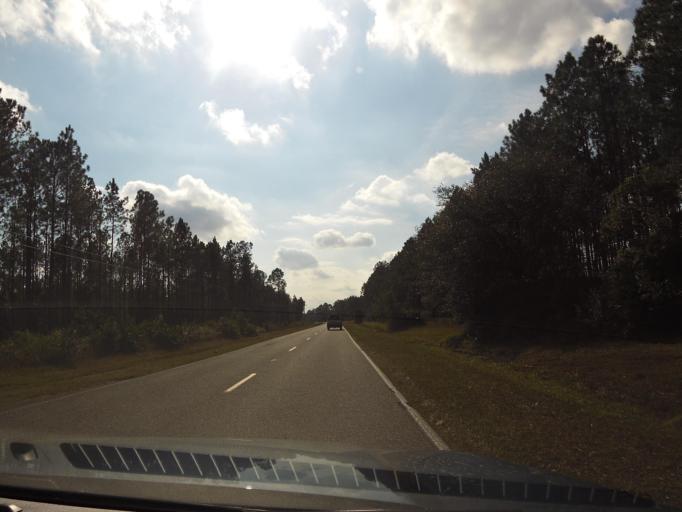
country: US
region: Florida
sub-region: Duval County
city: Baldwin
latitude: 30.1664
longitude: -81.9974
